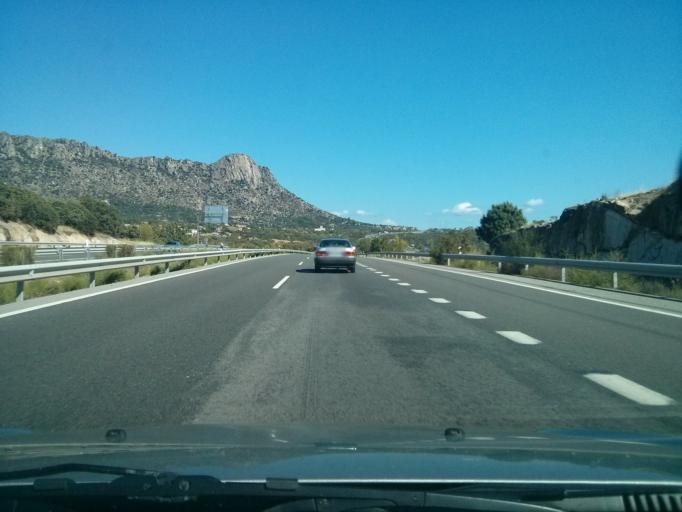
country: ES
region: Madrid
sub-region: Provincia de Madrid
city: La Cabrera
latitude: 40.8549
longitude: -3.6105
